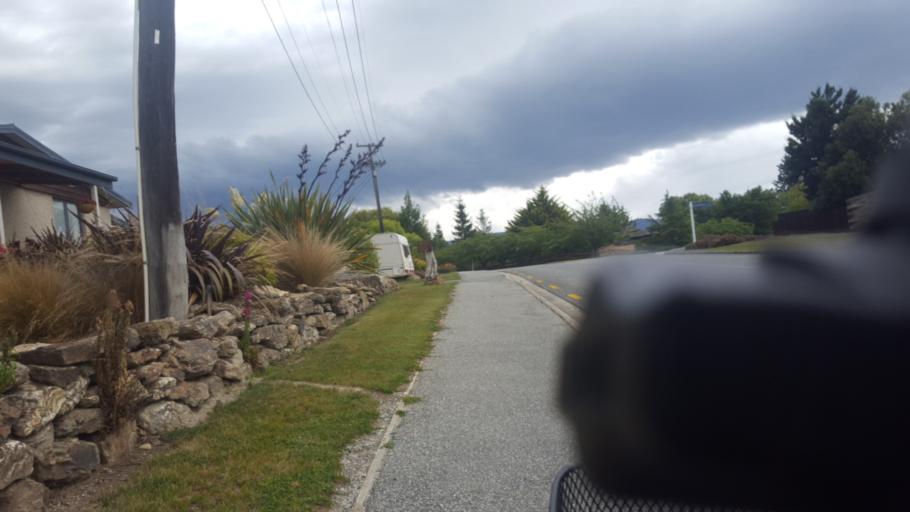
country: NZ
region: Otago
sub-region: Queenstown-Lakes District
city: Wanaka
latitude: -45.2596
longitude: 169.3810
